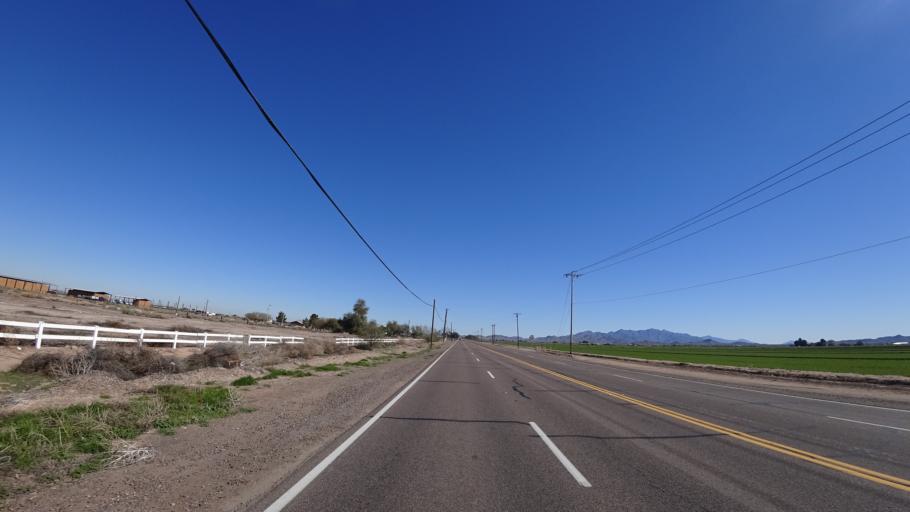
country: US
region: Arizona
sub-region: Maricopa County
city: Buckeye
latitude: 33.3776
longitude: -112.5030
